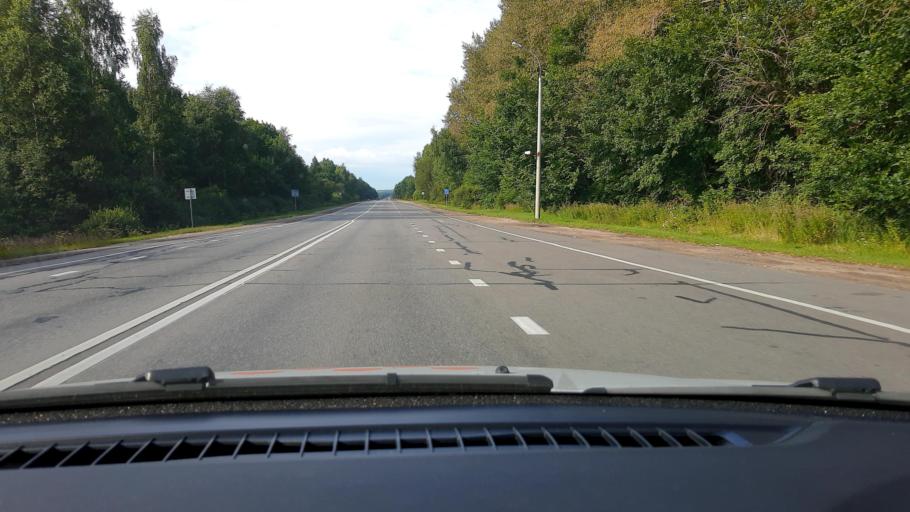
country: RU
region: Nizjnij Novgorod
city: Chernukha
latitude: 55.5670
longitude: 43.9587
